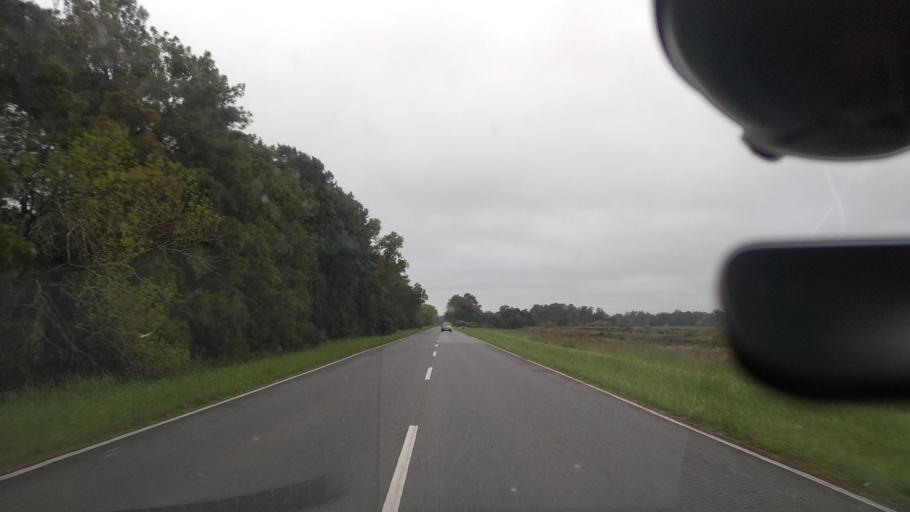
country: AR
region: Buenos Aires
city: Veronica
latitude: -35.4261
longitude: -57.3447
